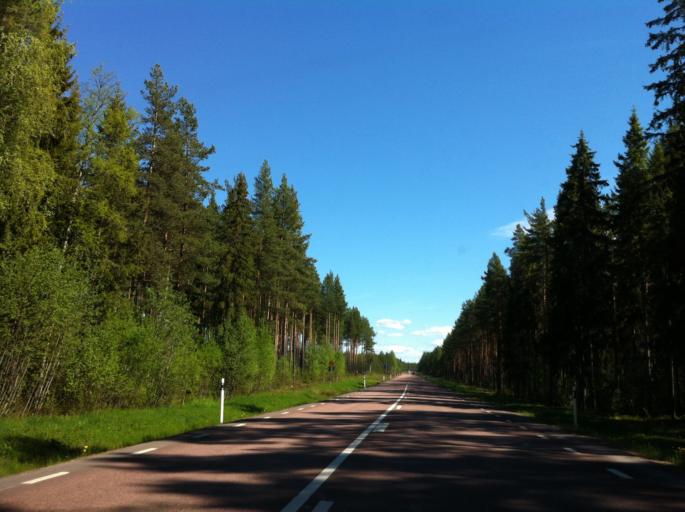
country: SE
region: Dalarna
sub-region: Mora Kommun
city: Mora
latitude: 60.9615
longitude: 14.6858
